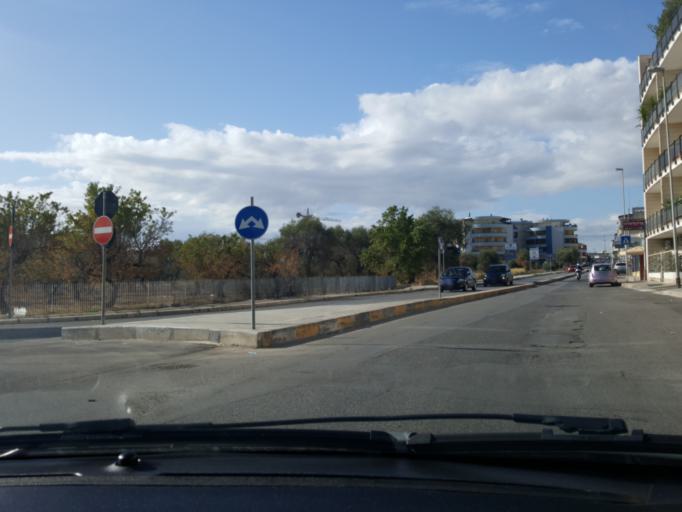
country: IT
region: Apulia
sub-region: Provincia di Bari
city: Triggiano
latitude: 41.0715
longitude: 16.9354
